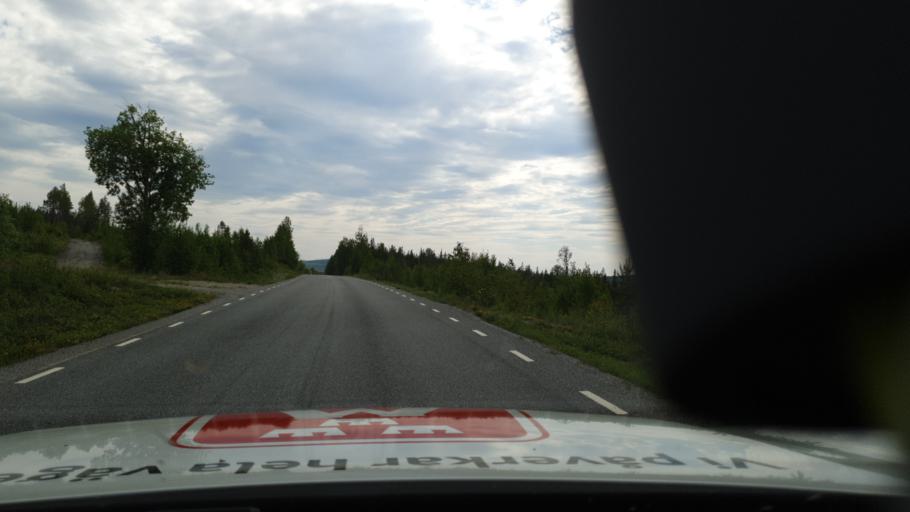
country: SE
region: Jaemtland
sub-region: Braecke Kommun
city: Braecke
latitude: 63.0946
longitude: 15.4394
